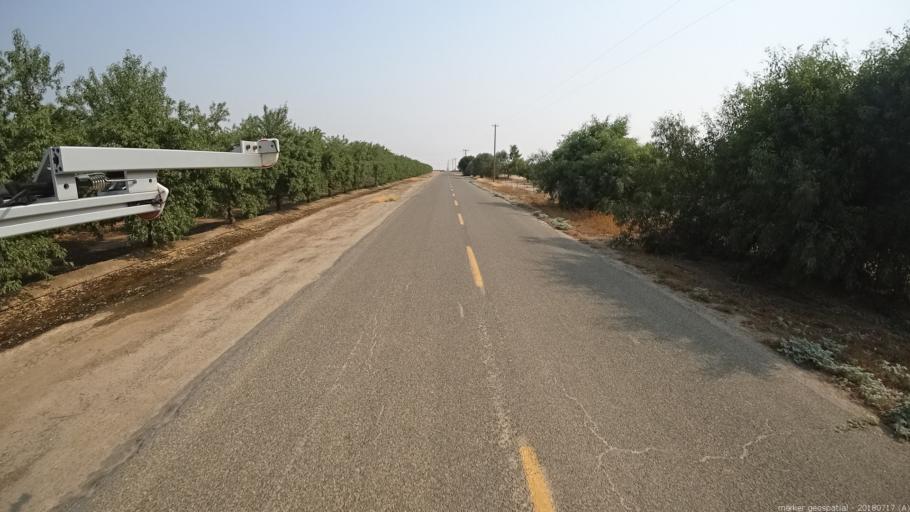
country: US
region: California
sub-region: Madera County
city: Fairmead
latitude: 37.1240
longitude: -120.1112
